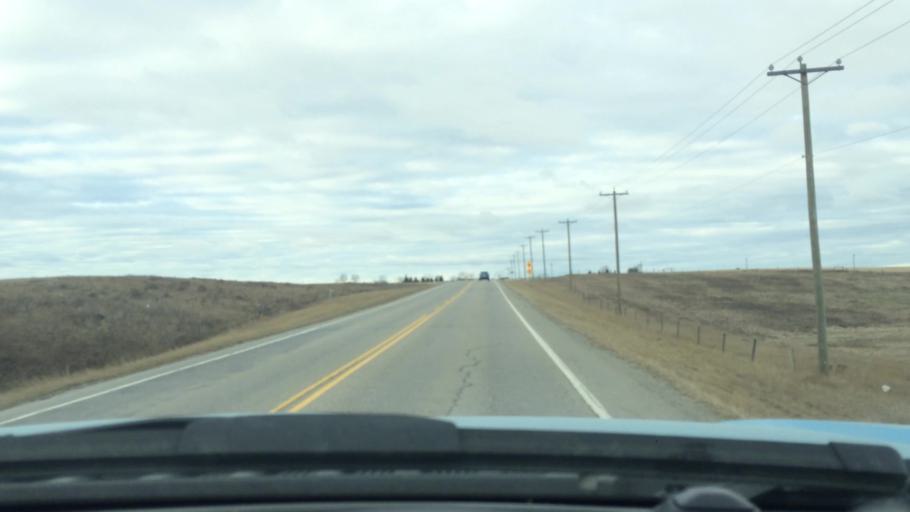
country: CA
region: Alberta
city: Airdrie
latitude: 51.2126
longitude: -114.0192
